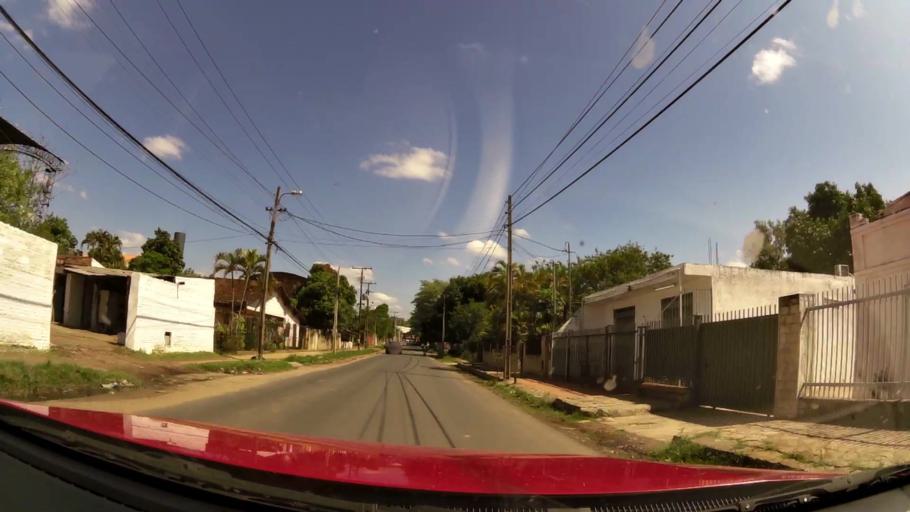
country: PY
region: Central
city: Colonia Mariano Roque Alonso
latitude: -25.2539
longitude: -57.5535
